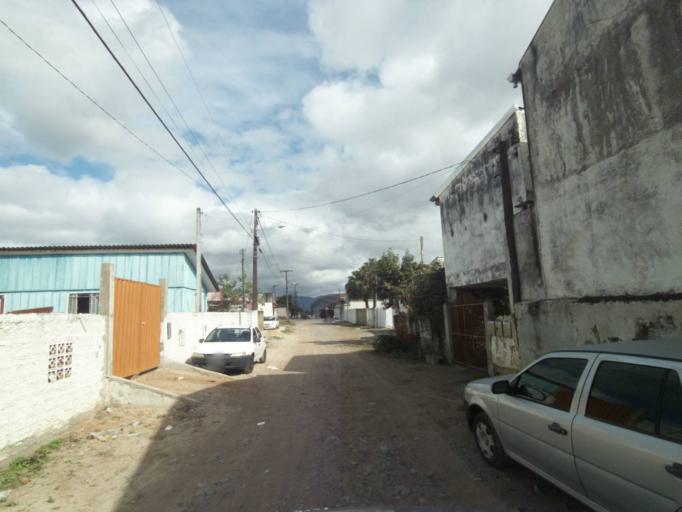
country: BR
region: Parana
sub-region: Paranagua
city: Paranagua
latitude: -25.5684
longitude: -48.5630
